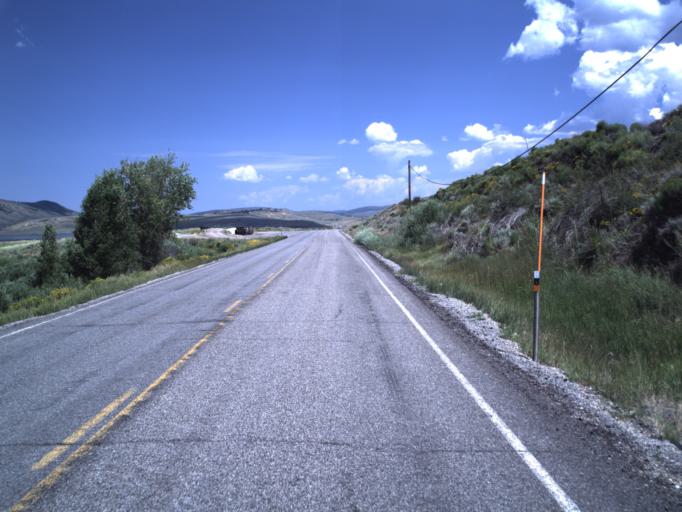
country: US
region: Utah
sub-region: Carbon County
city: Helper
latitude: 39.7473
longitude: -111.1508
